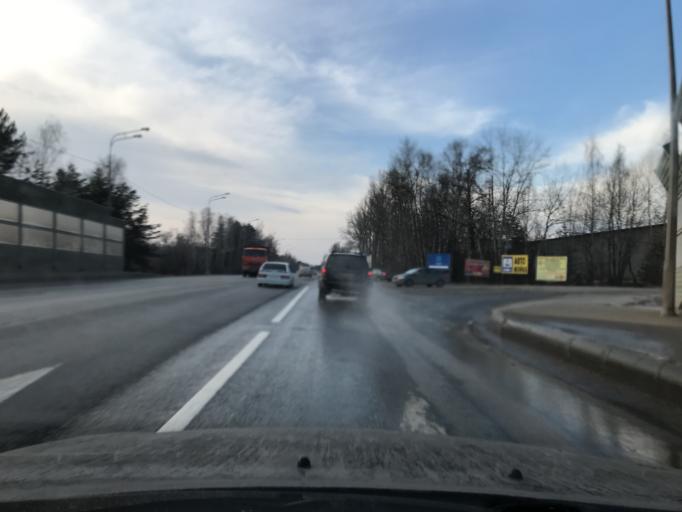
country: RU
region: Kaluga
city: Mstikhino
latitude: 54.5651
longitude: 36.1209
